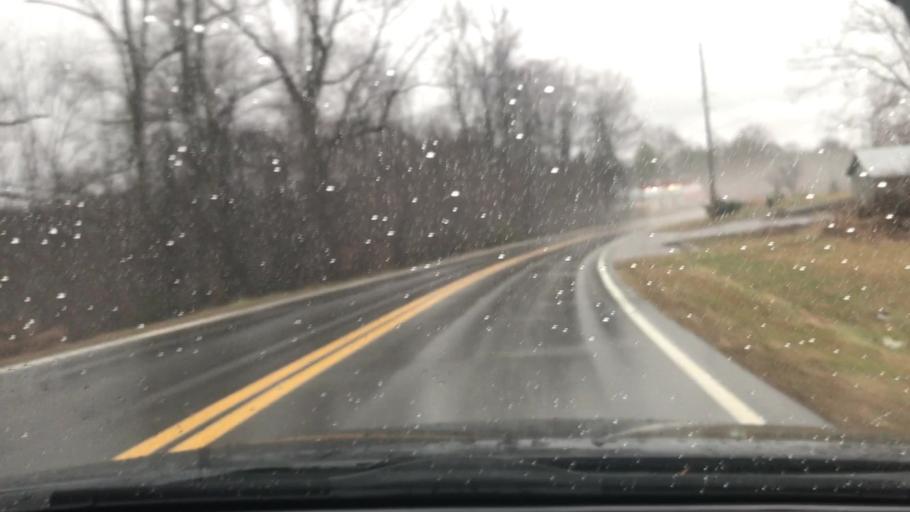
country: US
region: Tennessee
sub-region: Cheatham County
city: Ashland City
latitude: 36.2792
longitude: -87.1157
